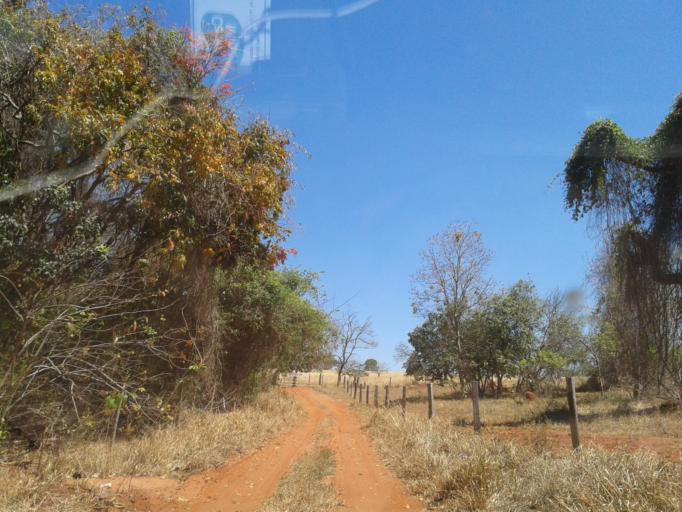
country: BR
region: Minas Gerais
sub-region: Ituiutaba
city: Ituiutaba
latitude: -19.1267
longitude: -49.3057
